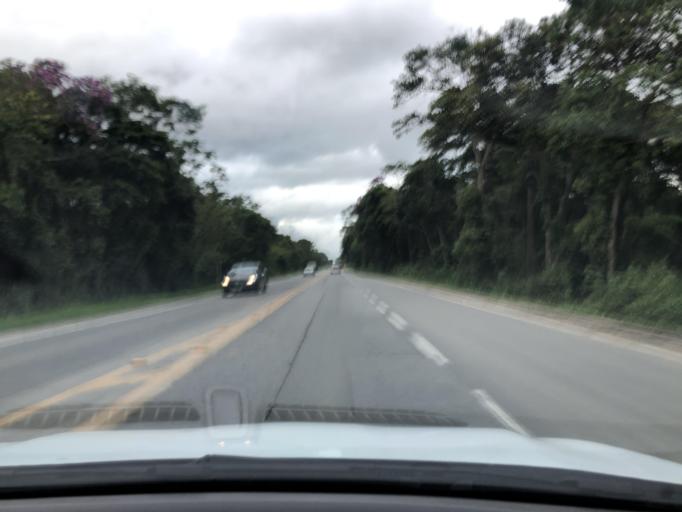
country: BR
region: Santa Catarina
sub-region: Sao Francisco Do Sul
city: Sao Francisco do Sul
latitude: -26.3305
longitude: -48.6516
